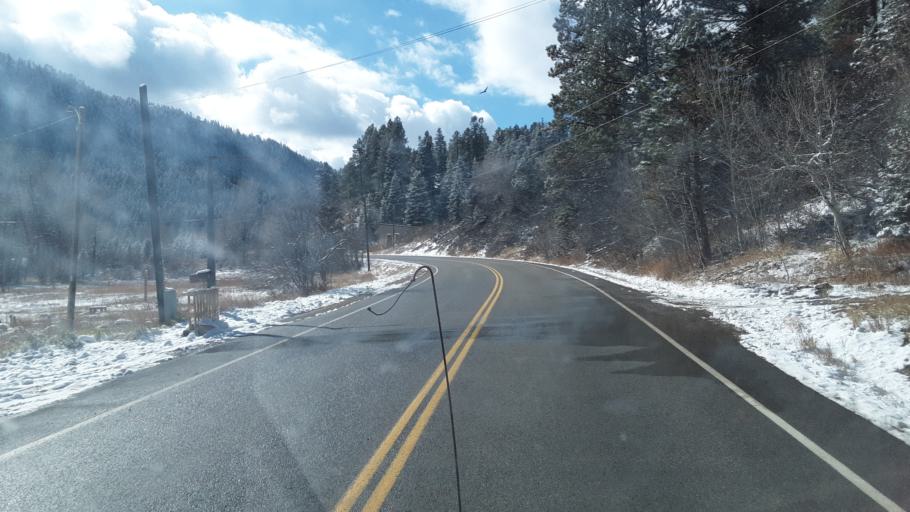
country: US
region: Colorado
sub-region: La Plata County
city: Bayfield
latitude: 37.3576
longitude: -107.6782
